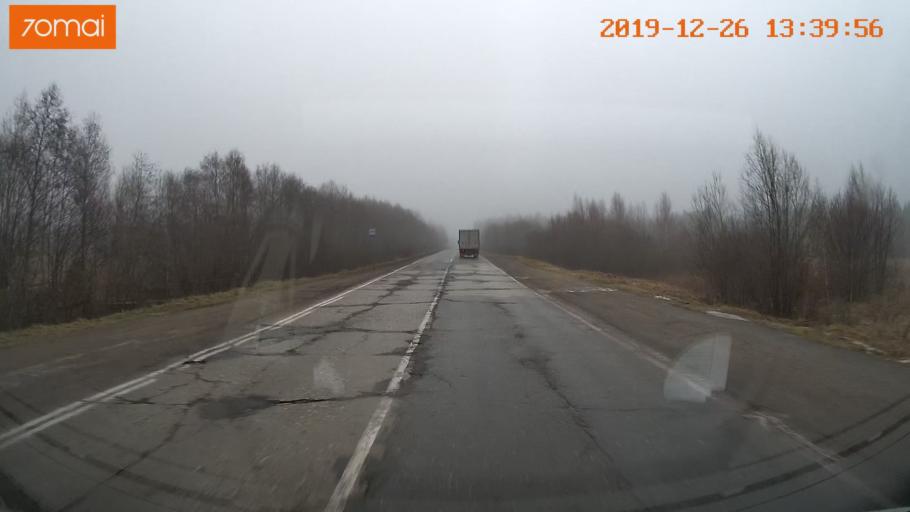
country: RU
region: Vologda
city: Sheksna
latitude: 58.7474
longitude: 38.4202
